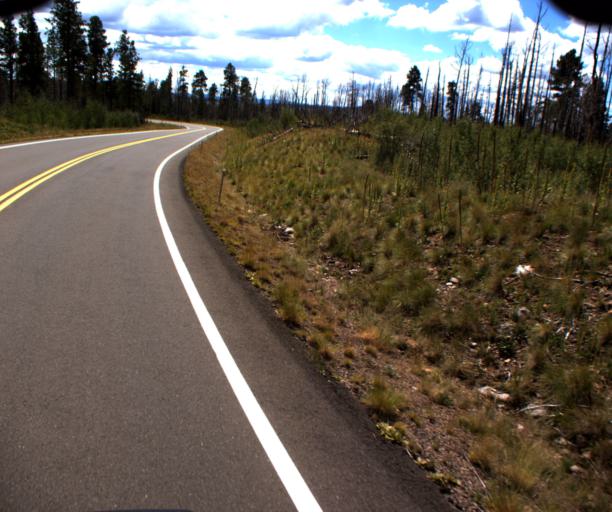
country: US
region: Arizona
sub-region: Apache County
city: Eagar
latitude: 33.9246
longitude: -109.4541
